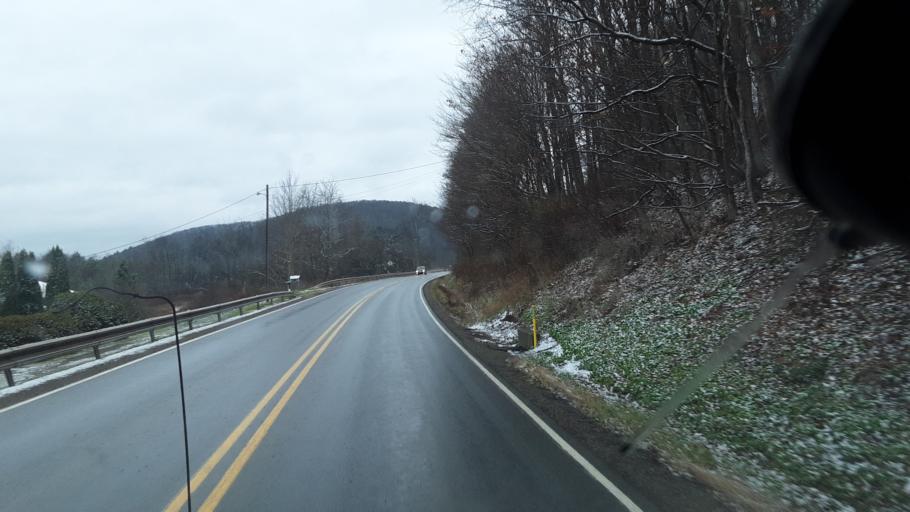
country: US
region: Pennsylvania
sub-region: Potter County
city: Coudersport
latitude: 41.8968
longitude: -78.0599
